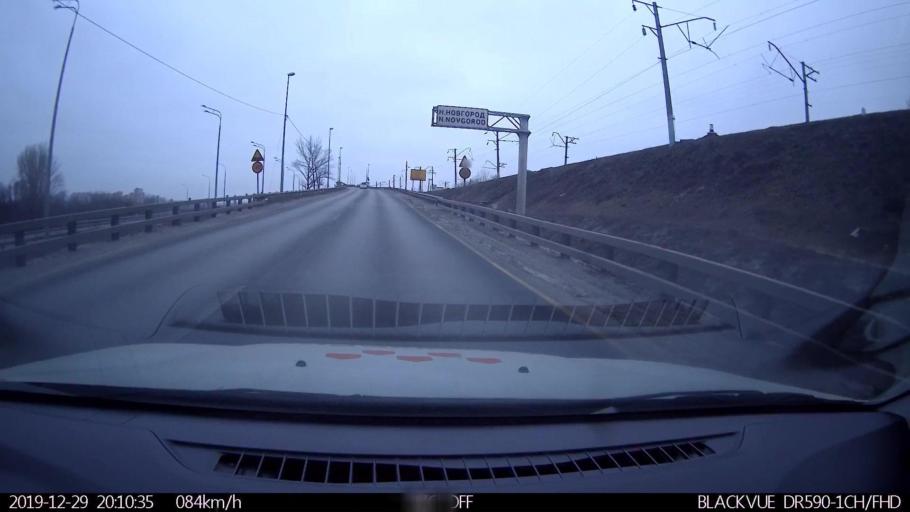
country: RU
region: Nizjnij Novgorod
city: Neklyudovo
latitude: 56.3643
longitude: 43.9346
